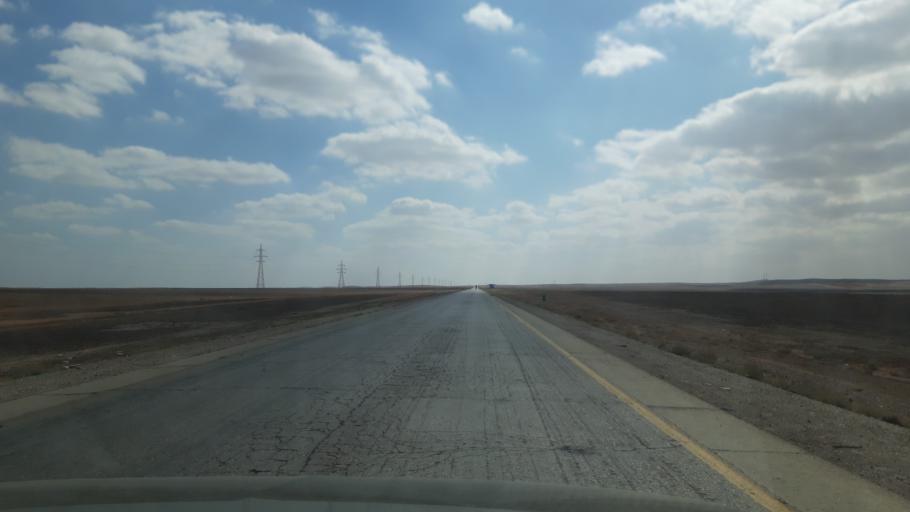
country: JO
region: Amman
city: Al Azraq ash Shamali
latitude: 31.7722
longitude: 36.5647
